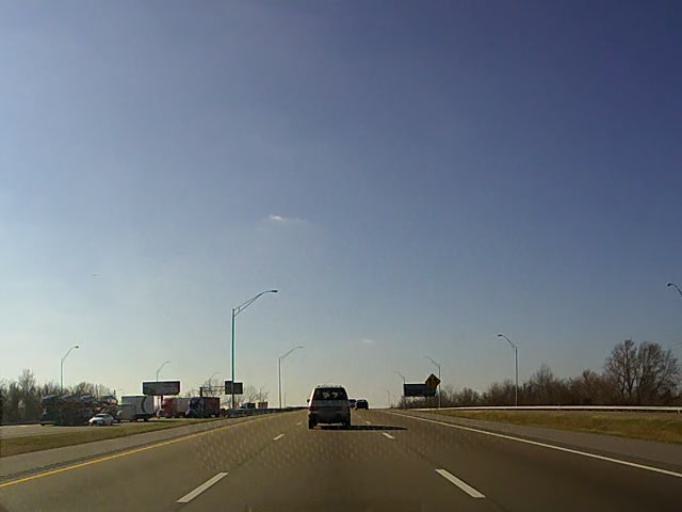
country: US
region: Tennessee
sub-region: Shelby County
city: New South Memphis
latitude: 35.0787
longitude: -89.9610
